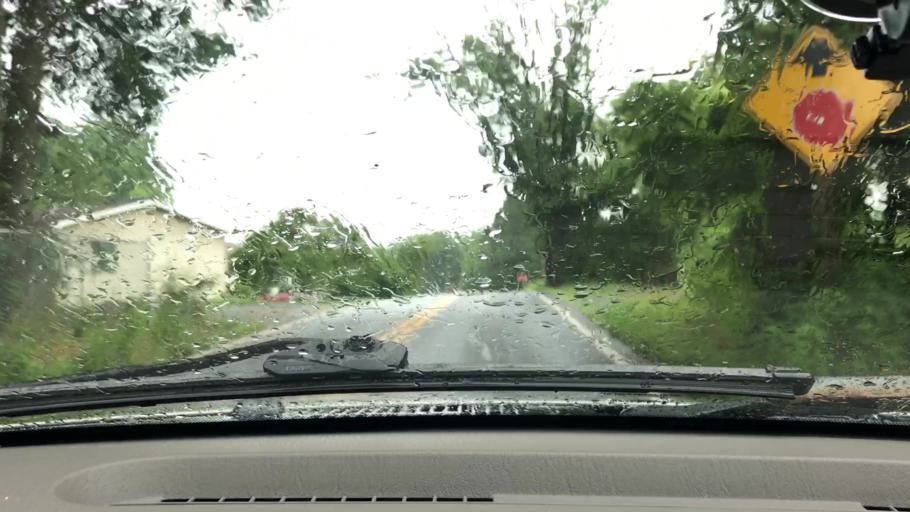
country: US
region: Pennsylvania
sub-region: Lancaster County
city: Elizabethtown
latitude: 40.2119
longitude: -76.6294
